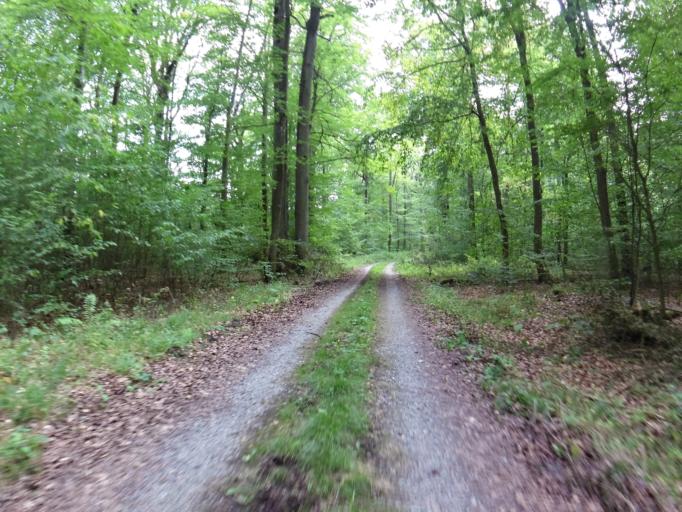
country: DE
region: Bavaria
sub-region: Regierungsbezirk Unterfranken
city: Kleinrinderfeld
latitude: 49.7075
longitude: 9.8221
